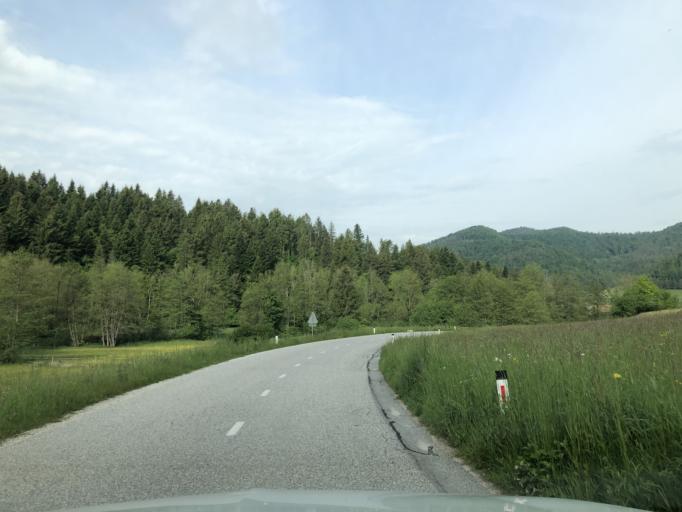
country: SI
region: Velike Lasce
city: Velike Lasce
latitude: 45.8077
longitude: 14.6141
